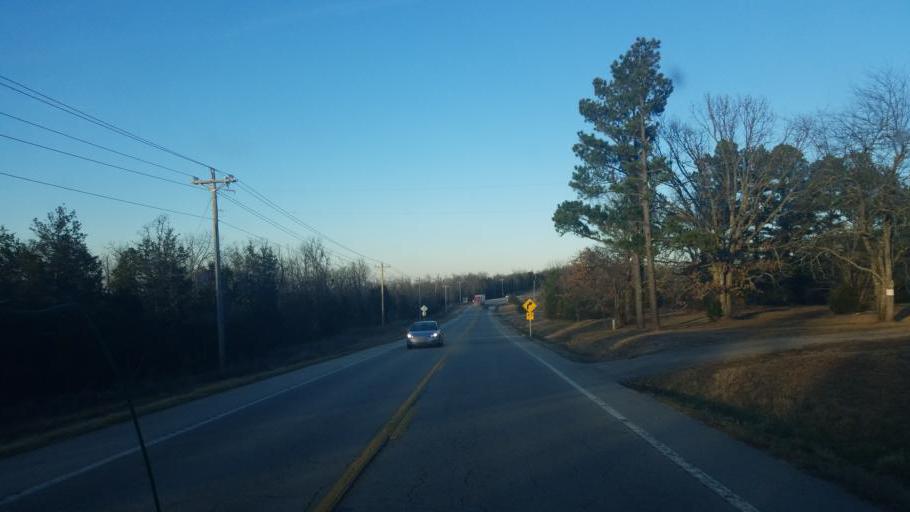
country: US
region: Arkansas
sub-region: Baxter County
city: Mountain Home
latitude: 36.3819
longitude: -92.1921
